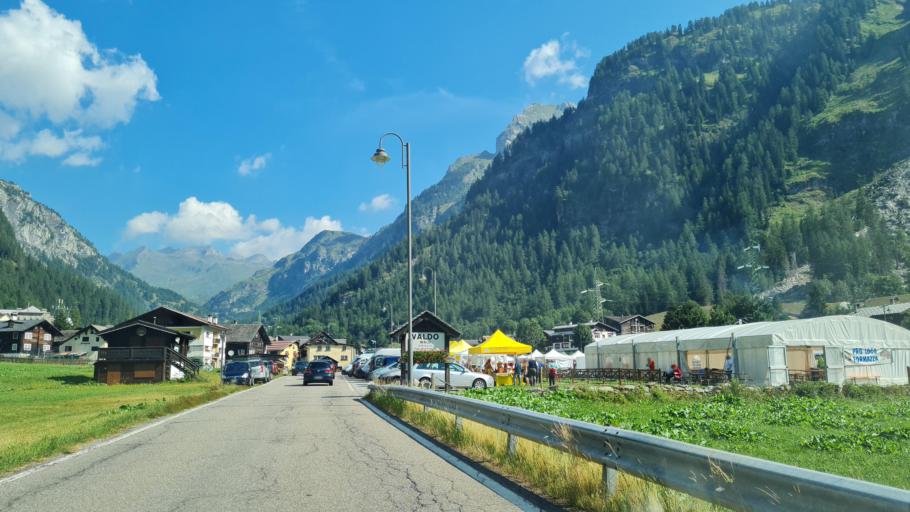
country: IT
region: Piedmont
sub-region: Provincia Verbano-Cusio-Ossola
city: Formazza
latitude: 46.3710
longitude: 8.4275
